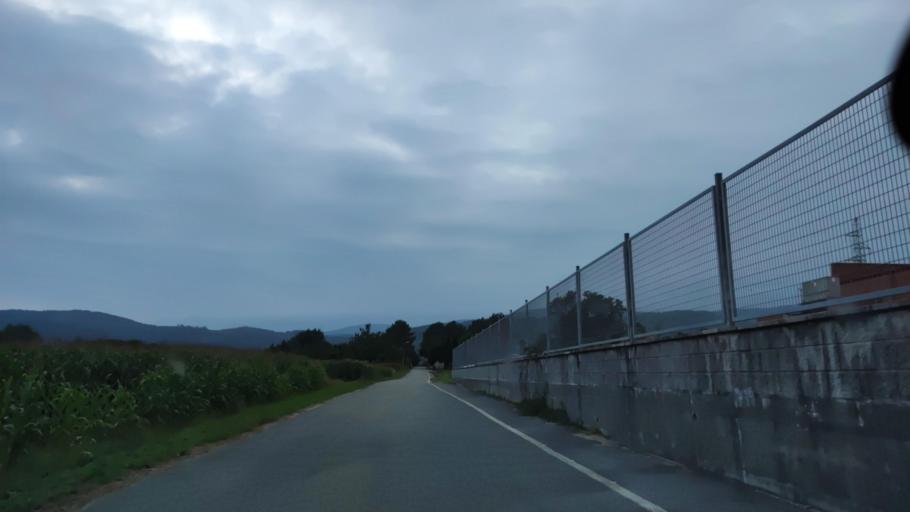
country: ES
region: Galicia
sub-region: Provincia da Coruna
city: Padron
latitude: 42.7136
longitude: -8.6980
